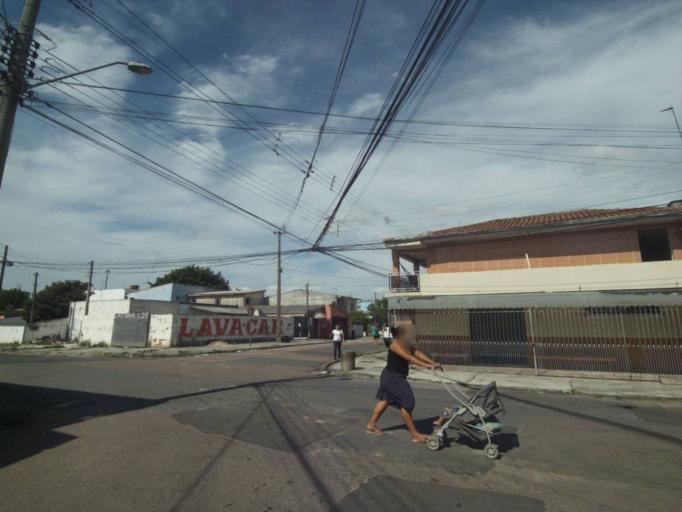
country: BR
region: Parana
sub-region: Curitiba
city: Curitiba
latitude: -25.5146
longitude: -49.3342
